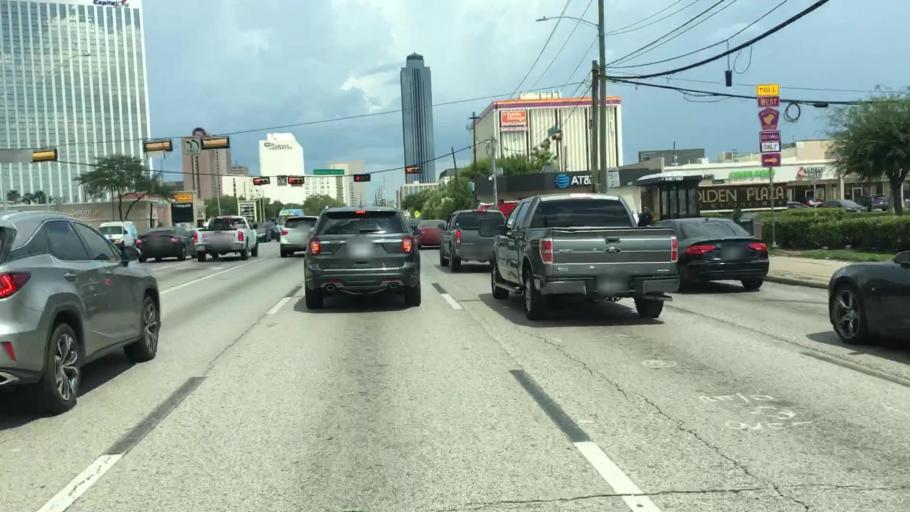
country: US
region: Texas
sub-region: Harris County
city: Bellaire
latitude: 29.7378
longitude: -95.4772
